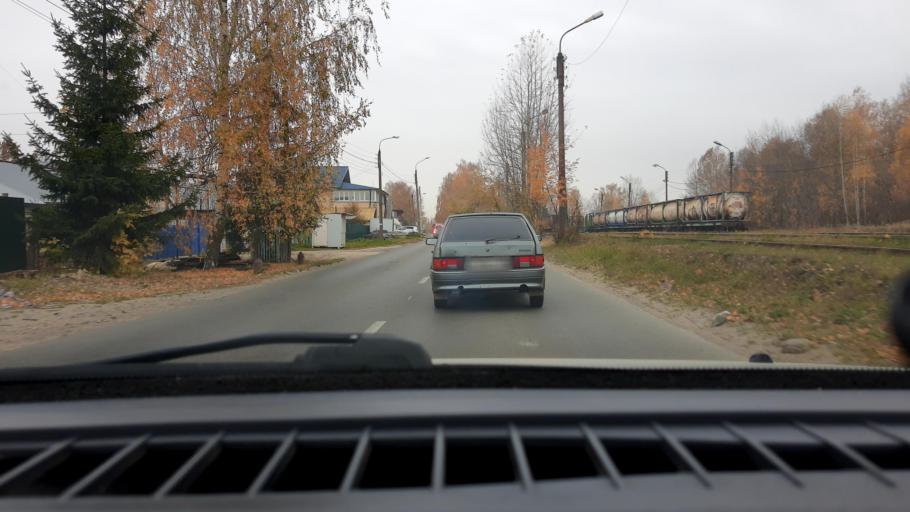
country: RU
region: Nizjnij Novgorod
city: Gorbatovka
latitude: 56.3480
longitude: 43.8318
